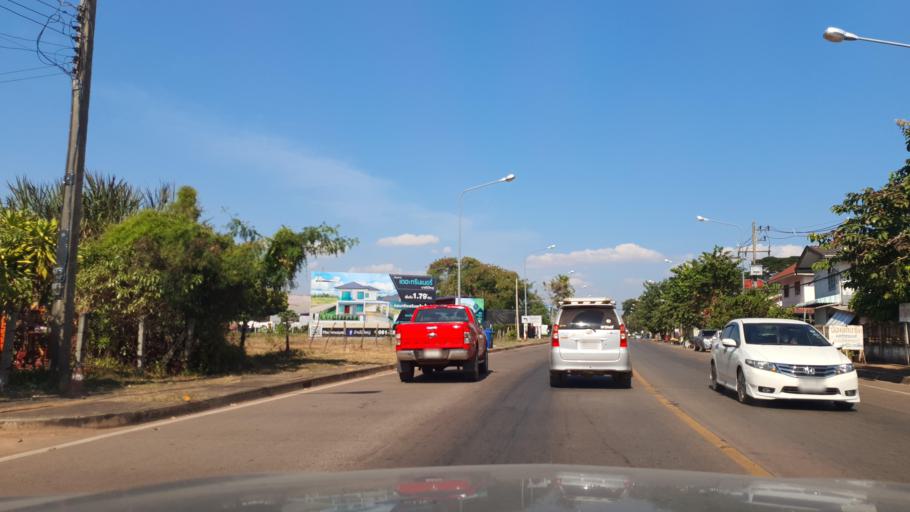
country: TH
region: Sakon Nakhon
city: Sakon Nakhon
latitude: 17.1586
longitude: 104.1262
